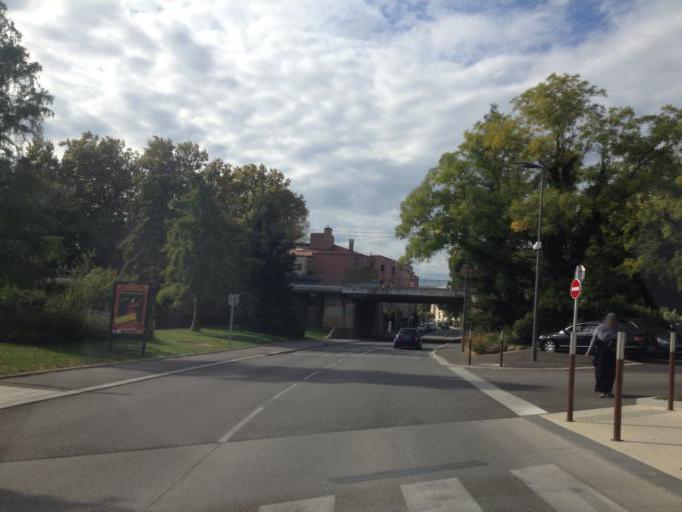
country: FR
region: Provence-Alpes-Cote d'Azur
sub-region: Departement du Vaucluse
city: Sorgues
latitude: 44.0075
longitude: 4.8777
